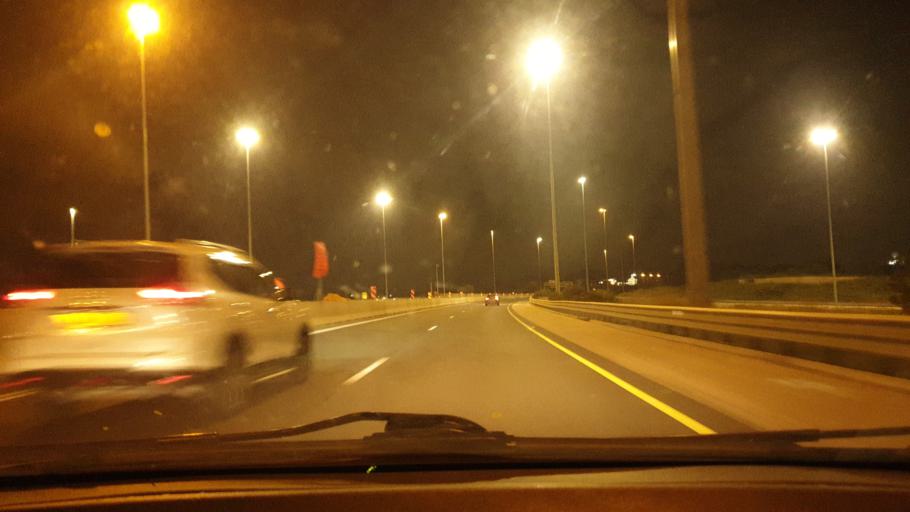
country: IL
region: Central District
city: Ramla
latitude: 31.9211
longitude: 34.8395
